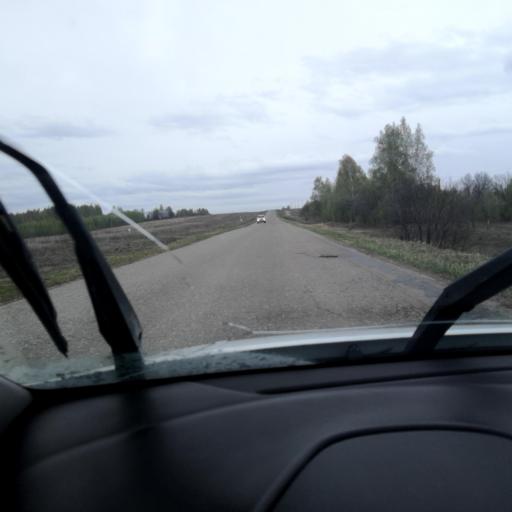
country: RU
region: Bashkortostan
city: Pavlovka
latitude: 55.3799
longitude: 56.4249
